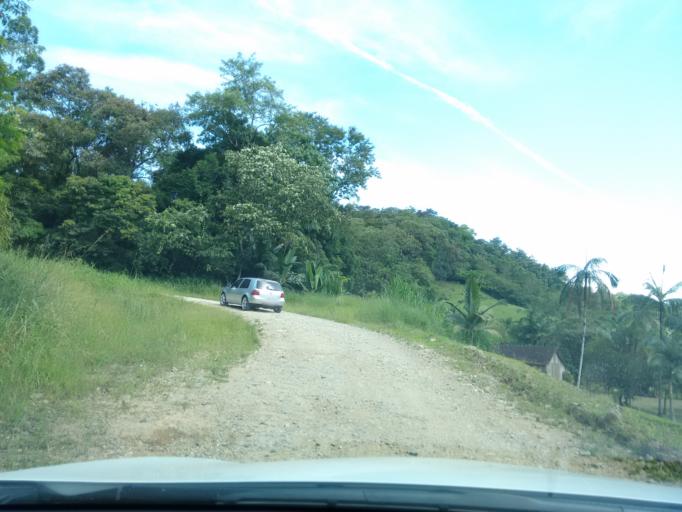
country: BR
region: Santa Catarina
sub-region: Pomerode
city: Pomerode
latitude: -26.7099
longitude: -49.0952
